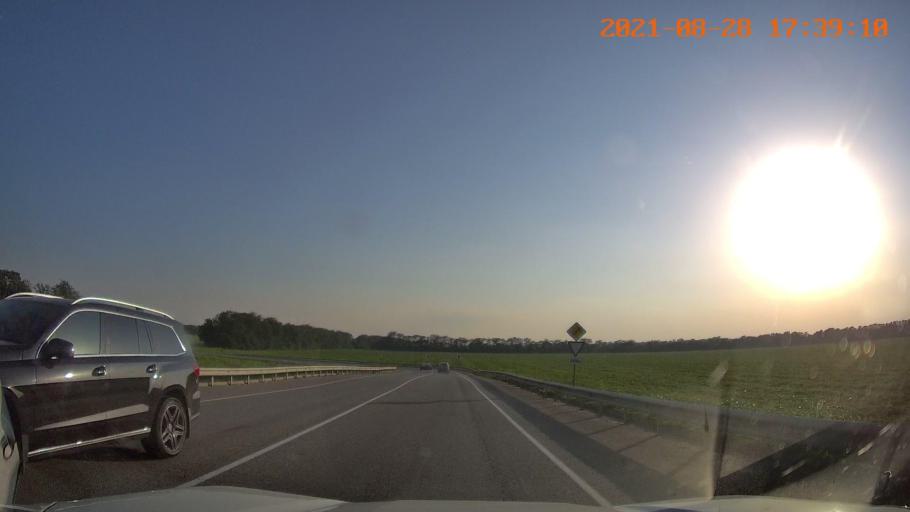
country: RU
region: Krasnodarskiy
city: Novokubansk
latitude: 45.0587
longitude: 40.9832
